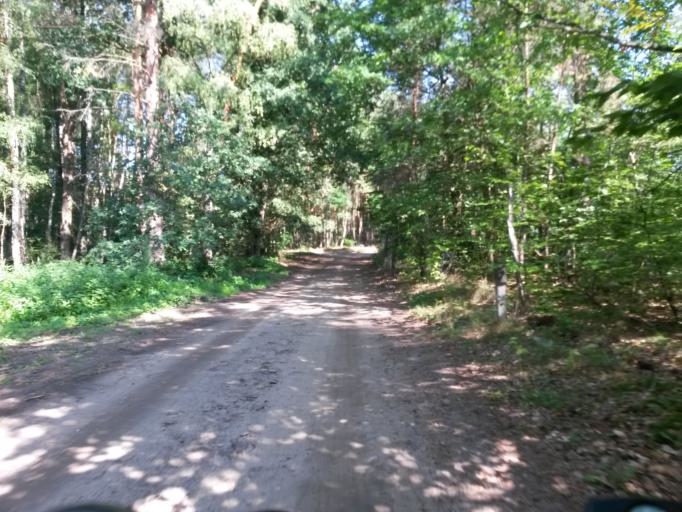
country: DE
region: Brandenburg
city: Zehdenick
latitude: 53.0405
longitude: 13.4086
